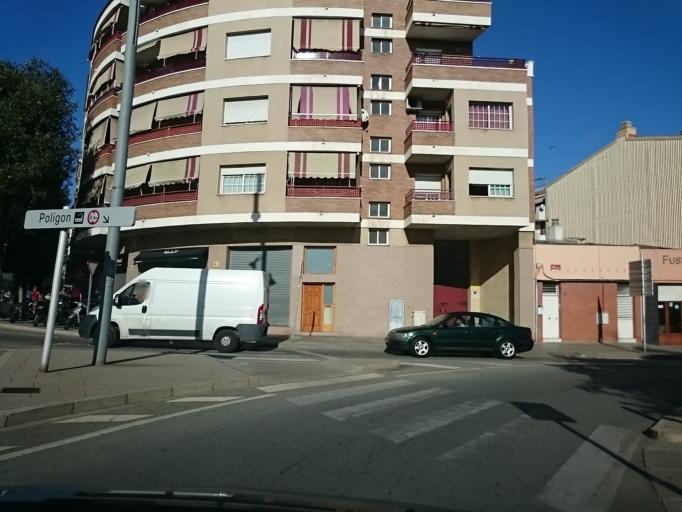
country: ES
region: Catalonia
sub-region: Provincia de Barcelona
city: Gava
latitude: 41.3019
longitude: 2.0069
